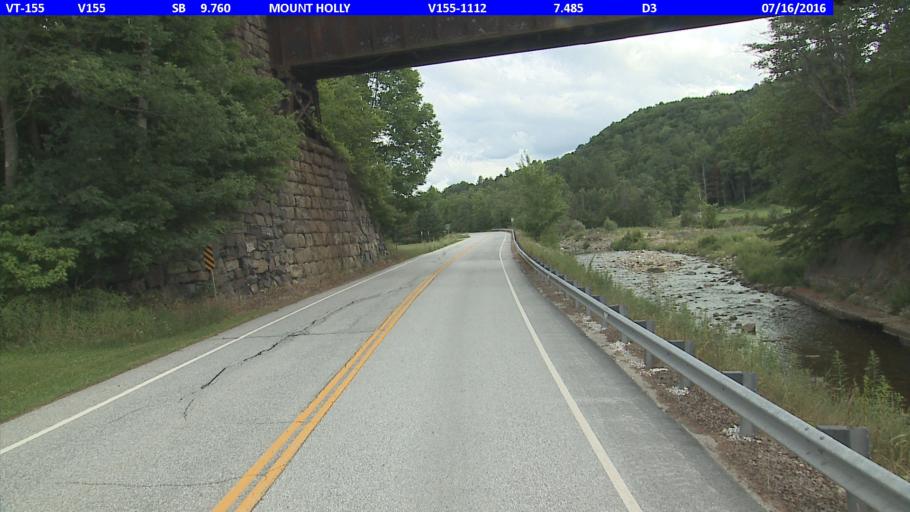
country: US
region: Vermont
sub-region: Rutland County
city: Rutland
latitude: 43.4465
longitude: -72.8715
